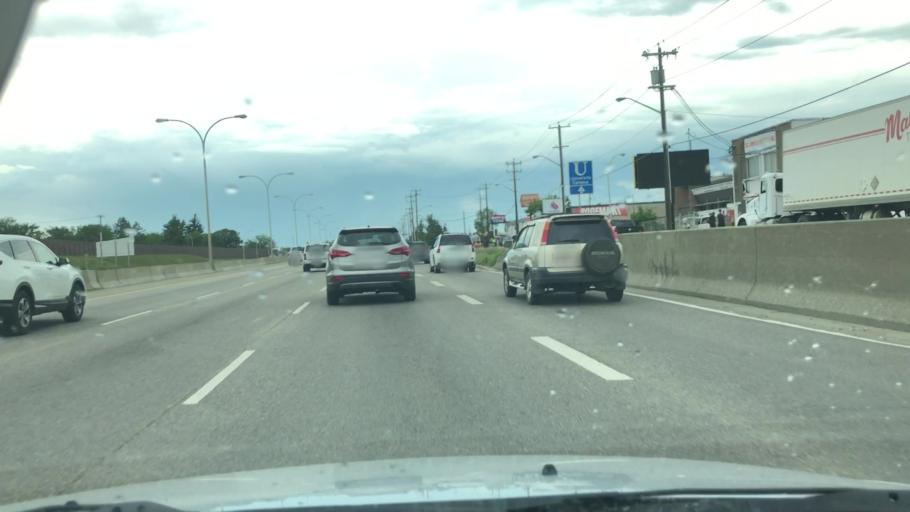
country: CA
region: Alberta
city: Edmonton
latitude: 53.5811
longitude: -113.4595
